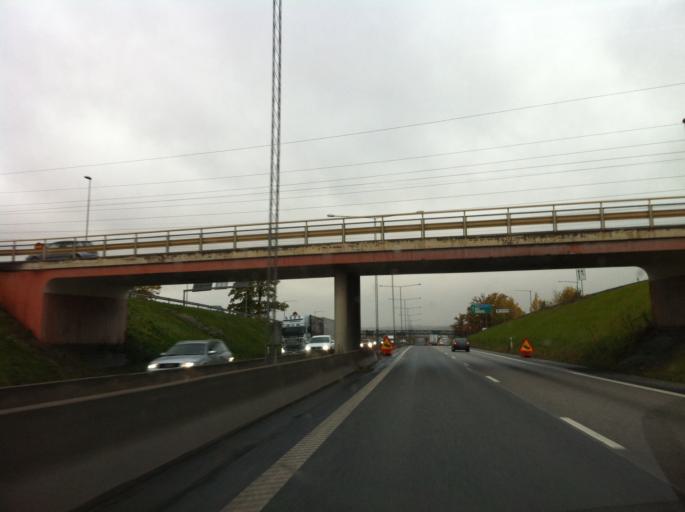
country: SE
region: Joenkoeping
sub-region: Jonkopings Kommun
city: Jonkoping
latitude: 57.7810
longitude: 14.2289
